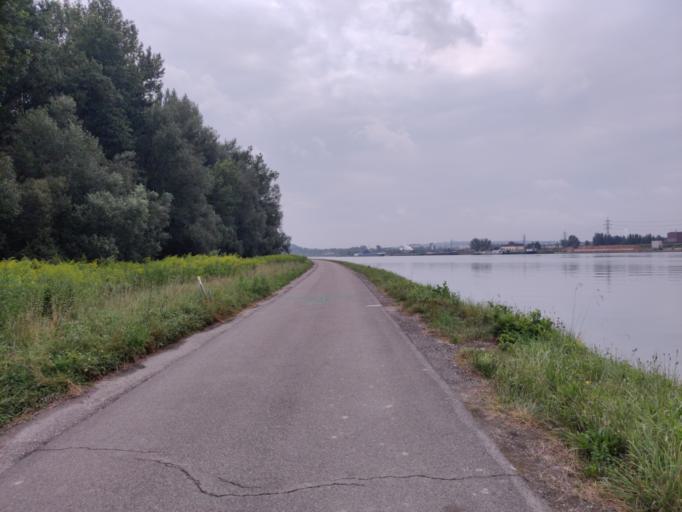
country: AT
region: Upper Austria
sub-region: Politischer Bezirk Urfahr-Umgebung
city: Steyregg
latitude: 48.2857
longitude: 14.3460
